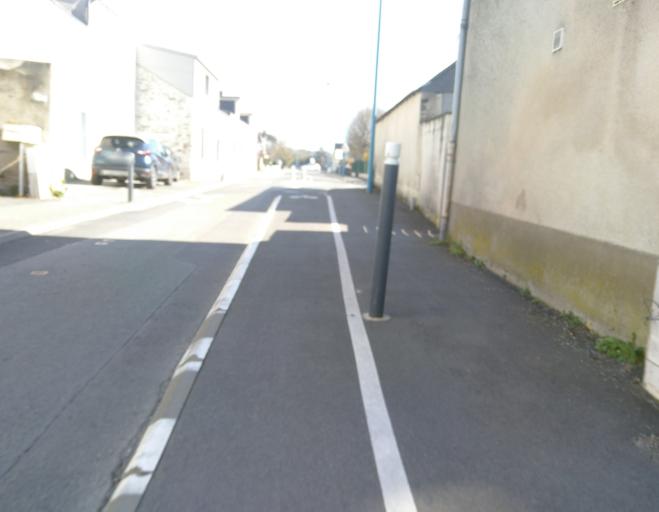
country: FR
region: Pays de la Loire
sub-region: Departement de Maine-et-Loire
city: Trelaze
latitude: 47.4625
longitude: -0.5001
